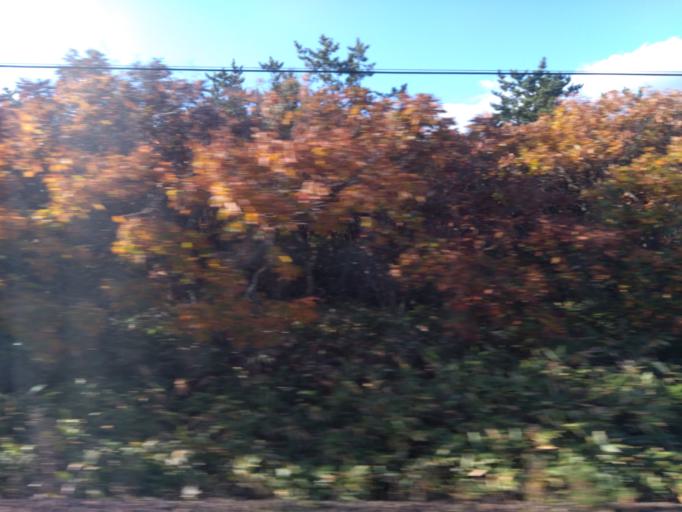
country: JP
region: Hokkaido
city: Niseko Town
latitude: 42.5619
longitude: 140.4314
